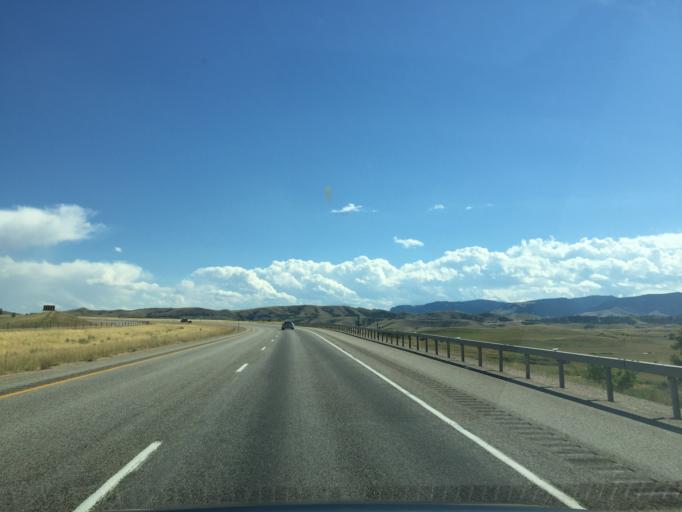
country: US
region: Wyoming
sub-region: Sheridan County
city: Sheridan
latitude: 44.6081
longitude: -106.8477
